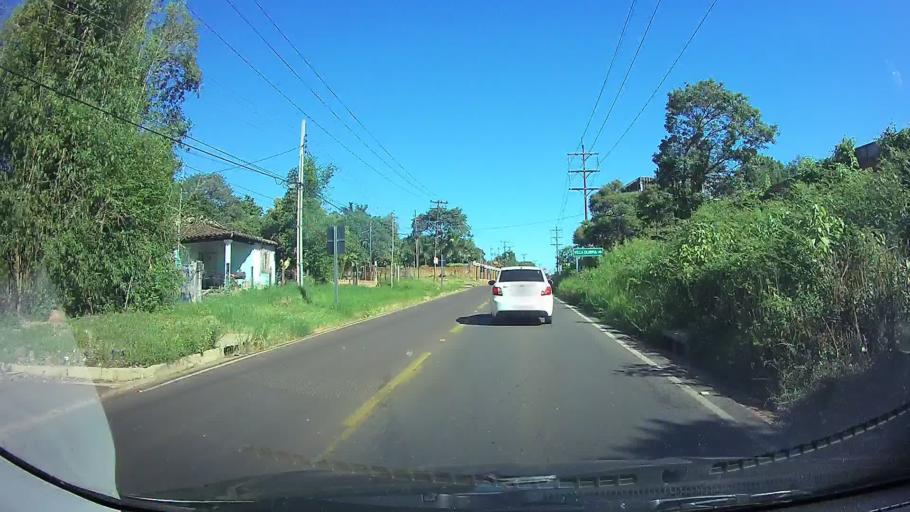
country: PY
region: Central
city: Fernando de la Mora
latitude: -25.3122
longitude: -57.5249
